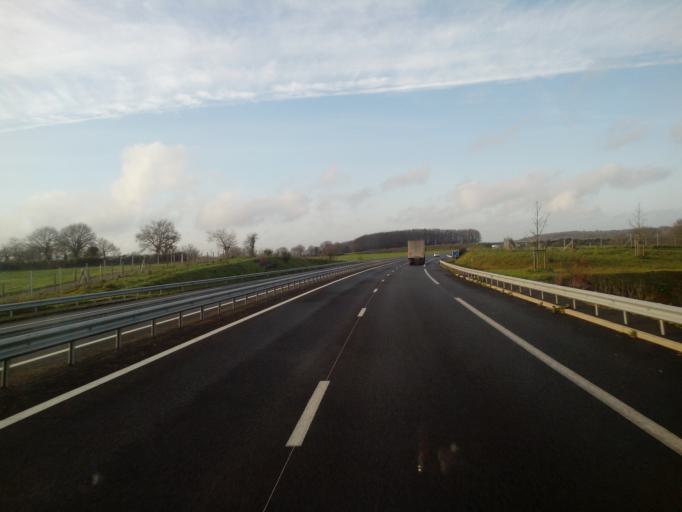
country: FR
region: Poitou-Charentes
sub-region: Departement des Deux-Sevres
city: Nueil-les-Aubiers
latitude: 46.8808
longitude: -0.5963
